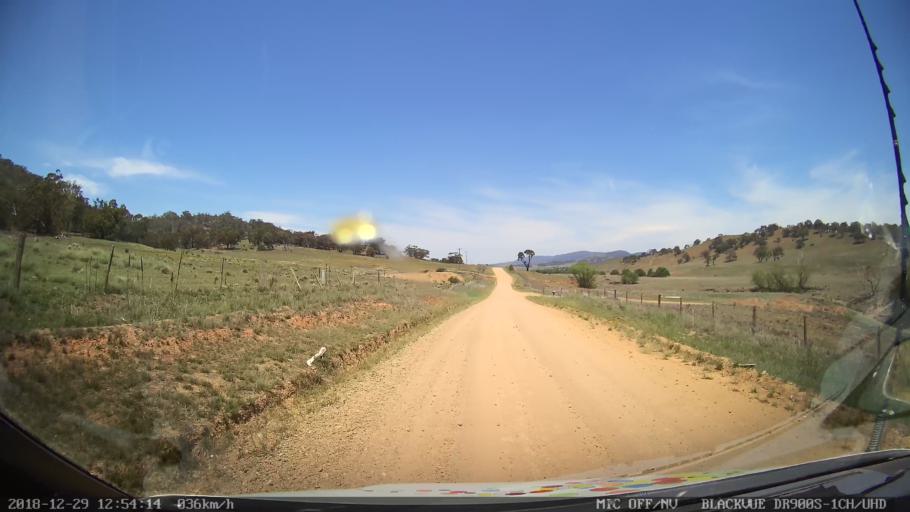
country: AU
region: Australian Capital Territory
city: Macarthur
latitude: -35.6900
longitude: 149.1872
